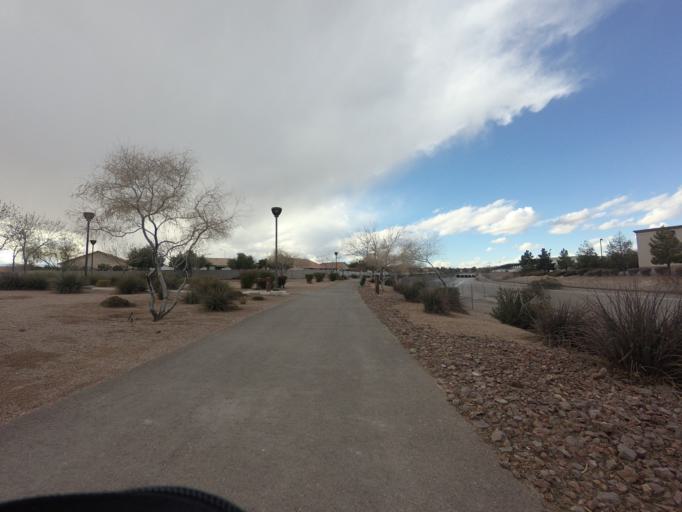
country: US
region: Nevada
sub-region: Clark County
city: North Las Vegas
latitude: 36.2582
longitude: -115.1816
